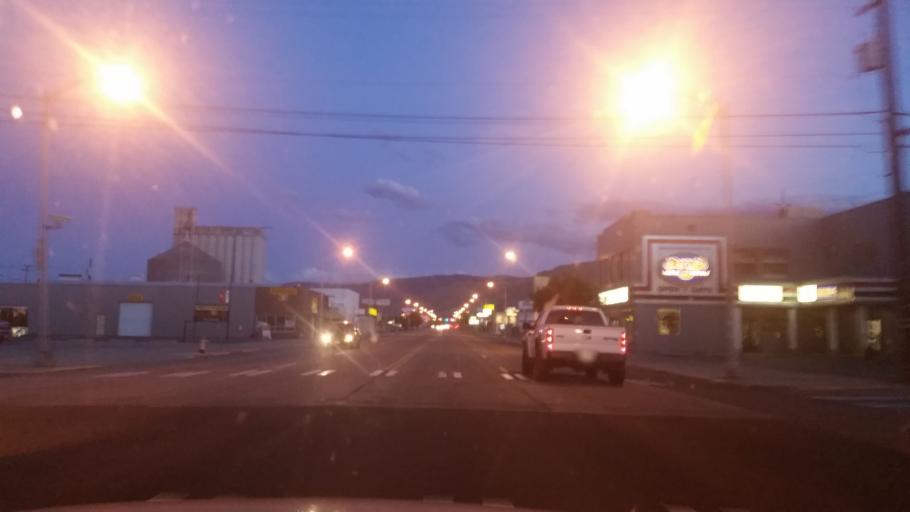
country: US
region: Washington
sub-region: Chelan County
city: Wenatchee
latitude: 47.4173
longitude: -120.3056
